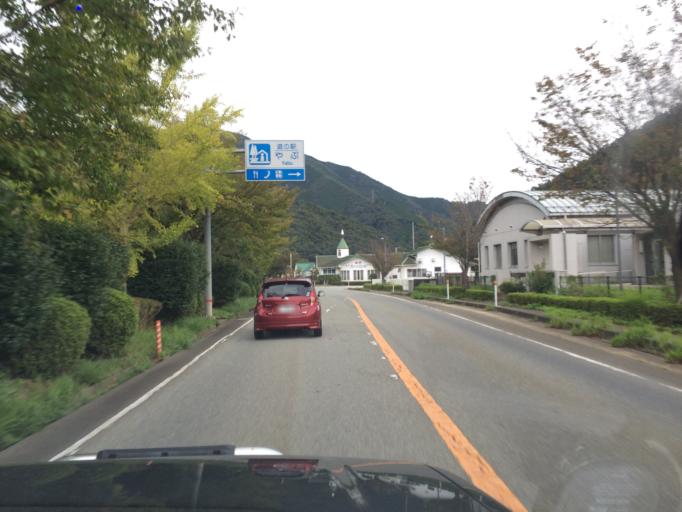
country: JP
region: Hyogo
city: Toyooka
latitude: 35.3812
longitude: 134.8153
